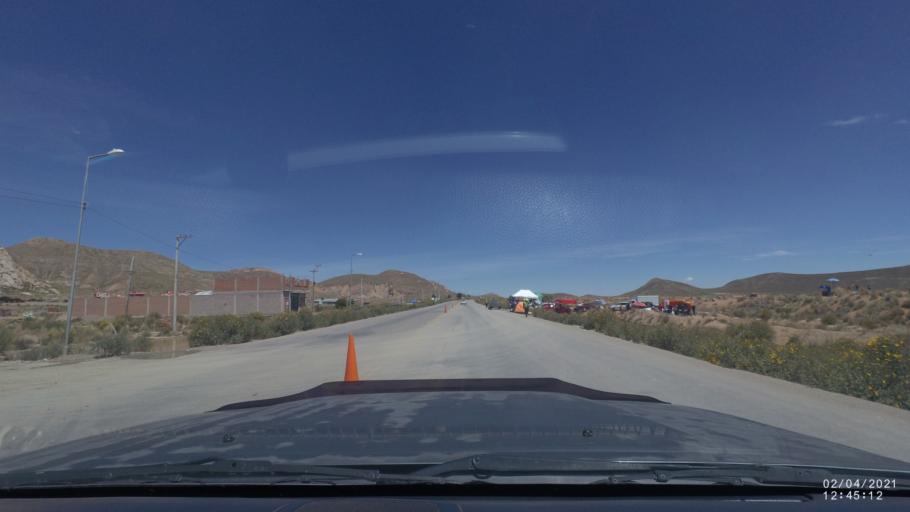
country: BO
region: Oruro
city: Oruro
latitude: -17.9334
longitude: -67.1324
